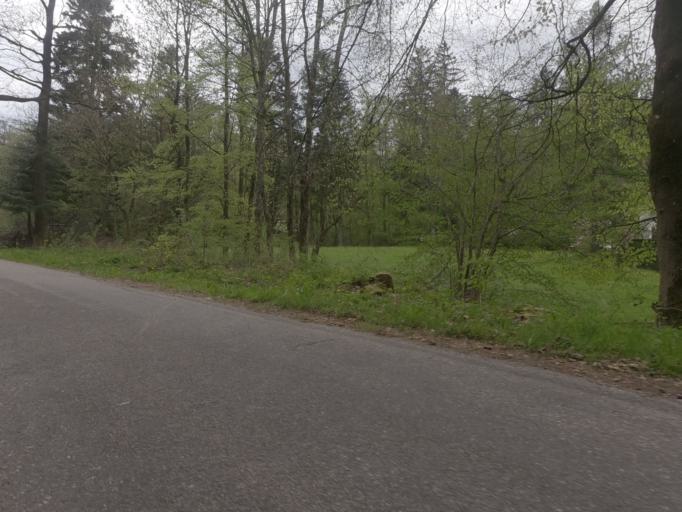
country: CH
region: Solothurn
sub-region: Bezirk Lebern
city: Riedholz
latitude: 47.2383
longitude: 7.5738
